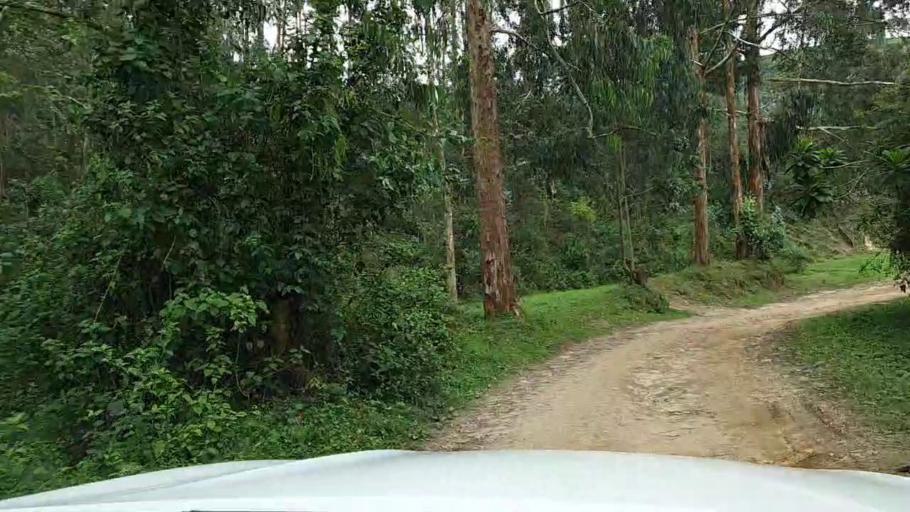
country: RW
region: Western Province
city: Kibuye
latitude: -2.2731
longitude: 29.3634
